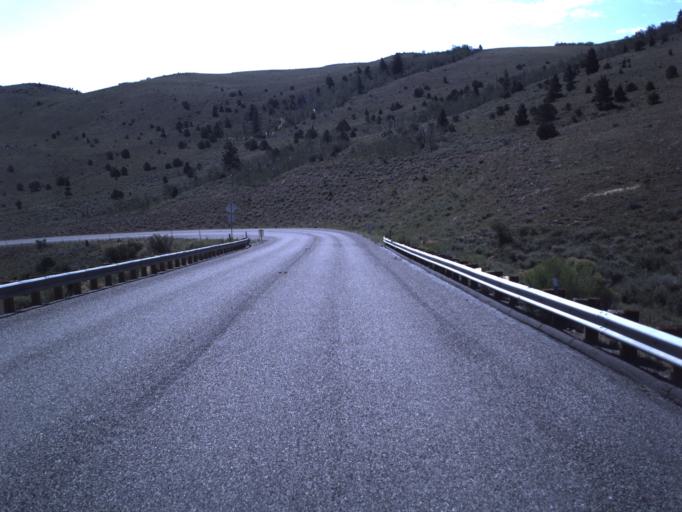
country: US
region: Utah
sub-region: Wayne County
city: Loa
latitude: 38.6010
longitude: -111.4644
